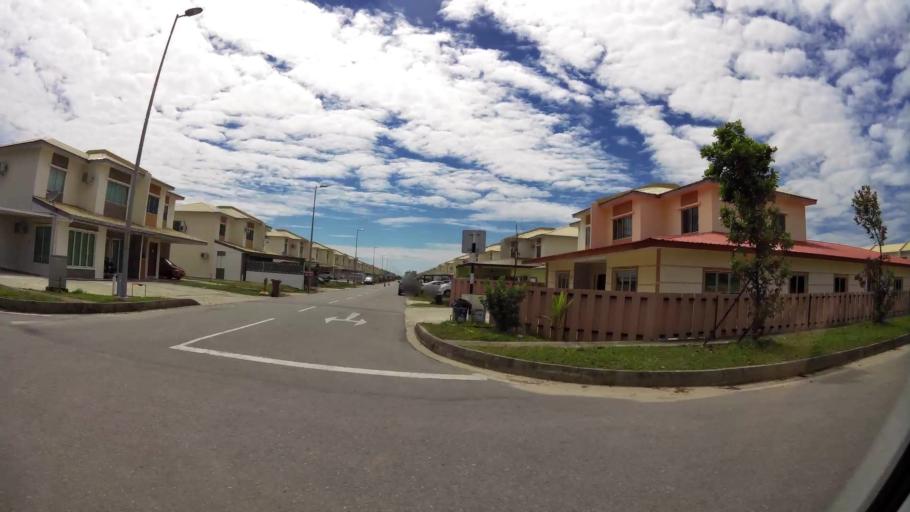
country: BN
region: Brunei and Muara
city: Bandar Seri Begawan
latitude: 4.9885
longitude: 115.0077
